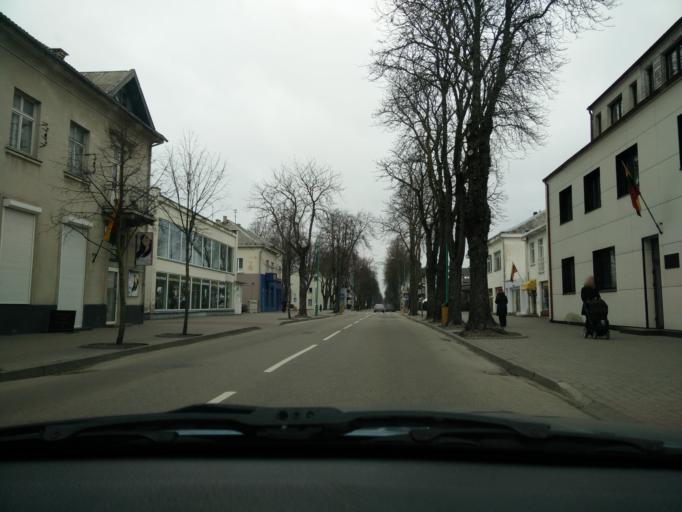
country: LT
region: Klaipedos apskritis
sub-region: Klaipeda
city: Palanga
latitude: 55.9193
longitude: 21.0673
